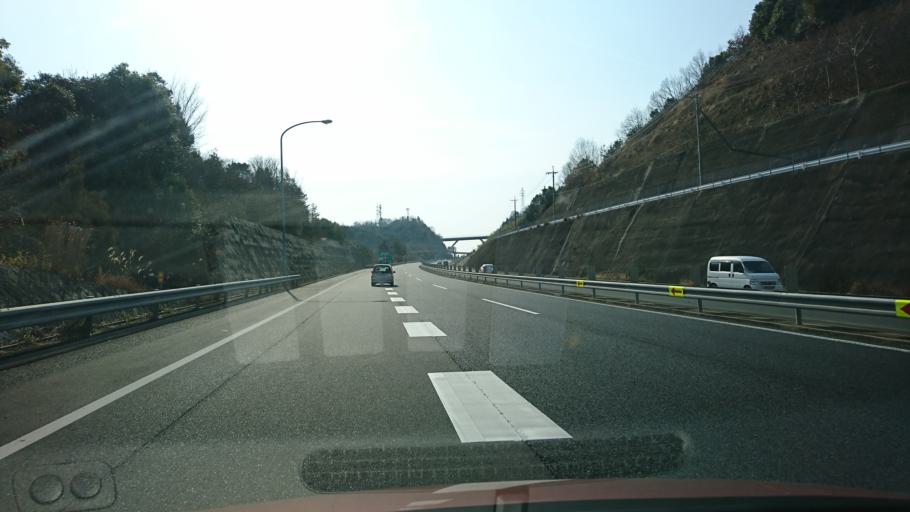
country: JP
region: Hiroshima
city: Onomichi
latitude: 34.4279
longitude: 133.2192
